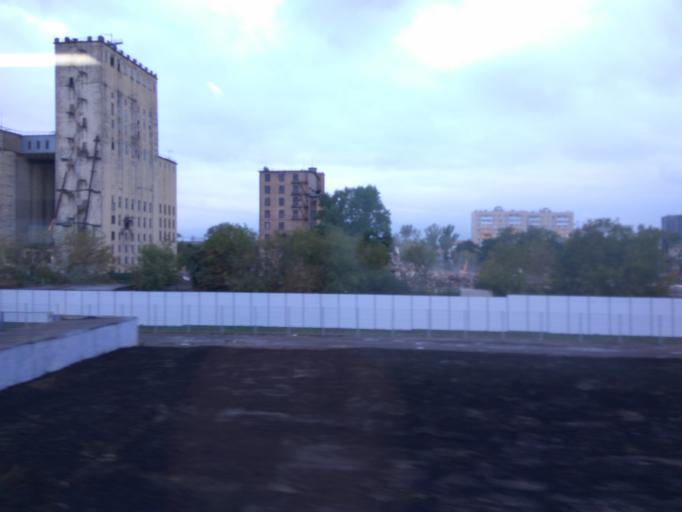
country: RU
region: Moskovskaya
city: Presnenskiy
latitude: 55.7540
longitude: 37.5280
